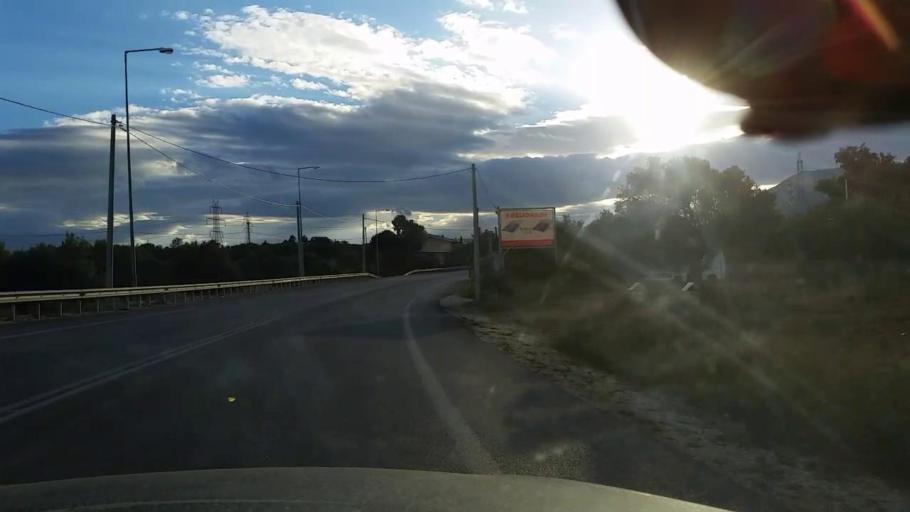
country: GR
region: Attica
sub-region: Nomarchia Anatolikis Attikis
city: Argithea
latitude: 37.9580
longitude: 23.8935
